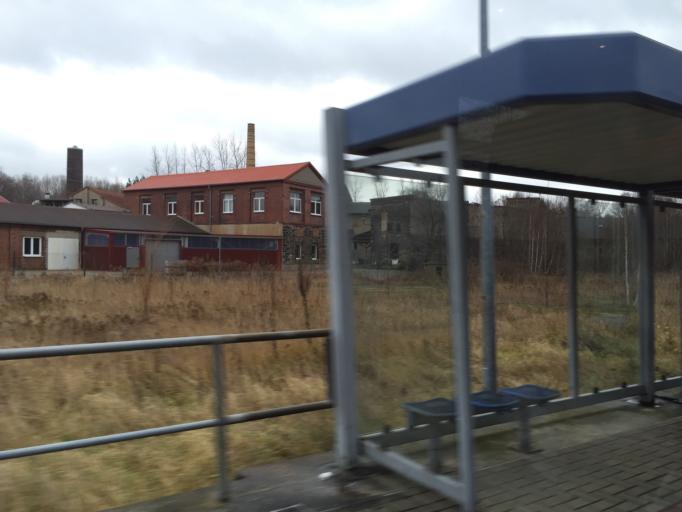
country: DE
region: Saxony
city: Reichenbach
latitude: 51.1357
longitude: 14.7955
